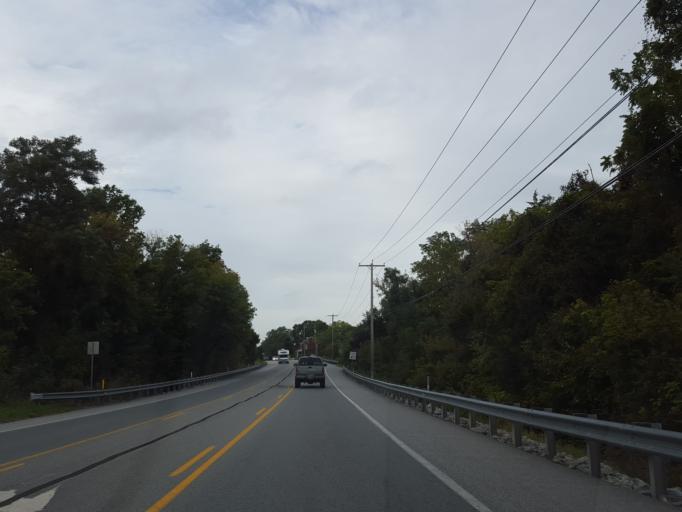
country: US
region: Pennsylvania
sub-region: Adams County
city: Abbottstown
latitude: 39.9028
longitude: -76.9461
